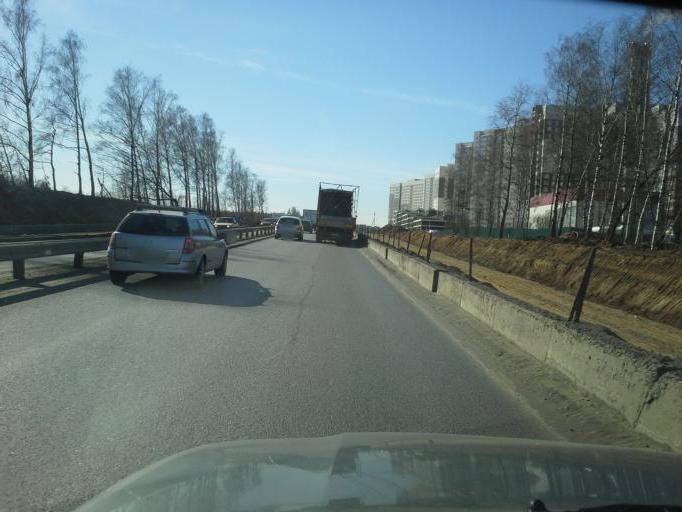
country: RU
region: Moskovskaya
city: Odintsovo
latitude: 55.6652
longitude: 37.3064
